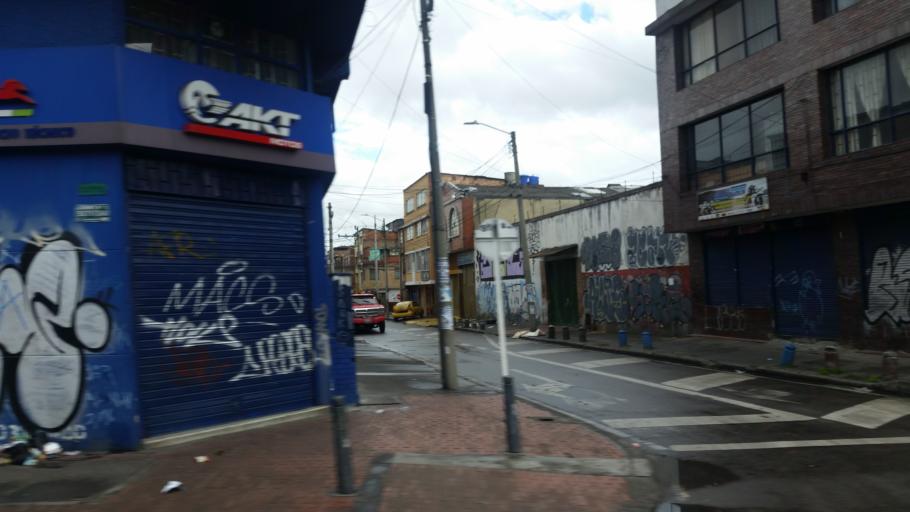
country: CO
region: Bogota D.C.
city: Bogota
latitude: 4.5819
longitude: -74.1016
